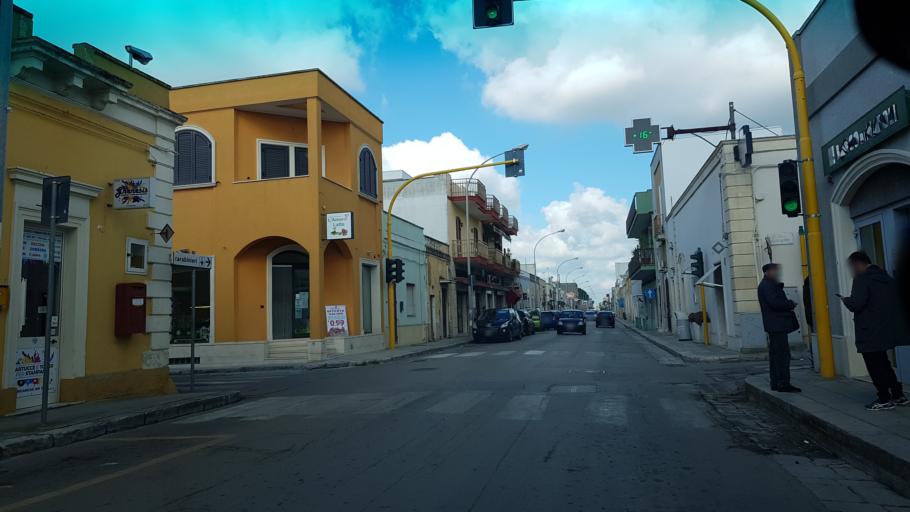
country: IT
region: Apulia
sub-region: Provincia di Lecce
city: Squinzano
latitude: 40.4351
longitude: 18.0406
